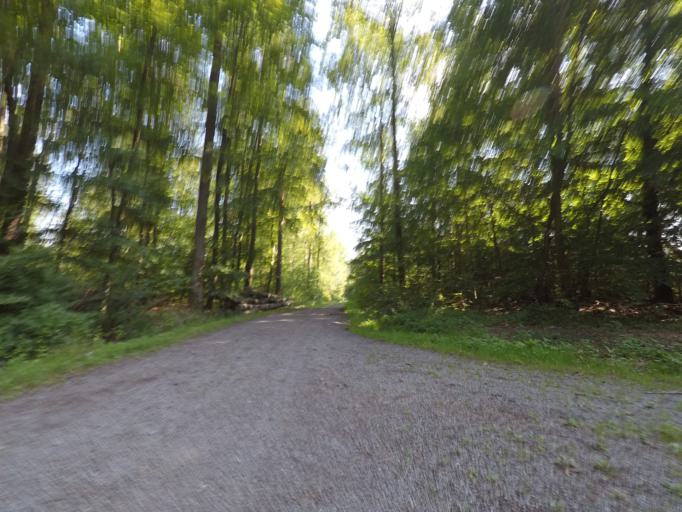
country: DE
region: Baden-Wuerttemberg
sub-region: Regierungsbezirk Stuttgart
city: Ehningen
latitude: 48.6683
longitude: 8.9765
